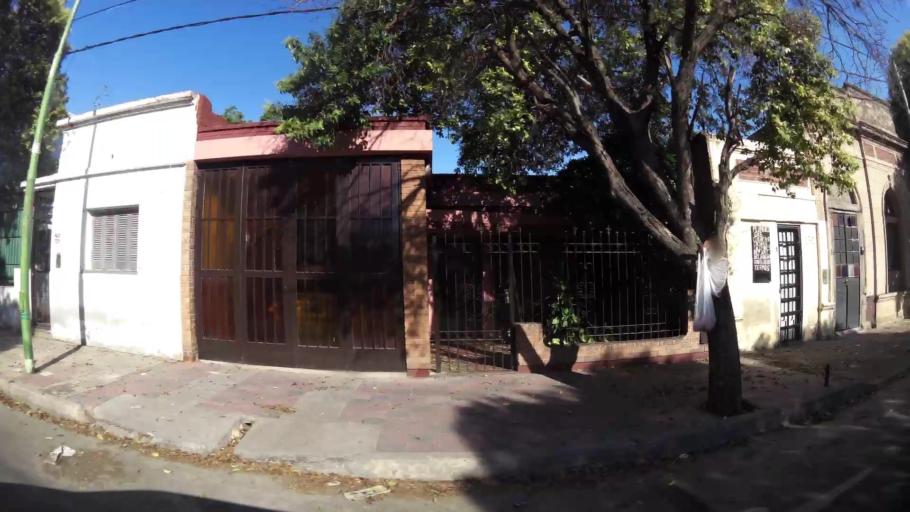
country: AR
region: Cordoba
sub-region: Departamento de Capital
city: Cordoba
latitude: -31.3930
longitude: -64.1720
